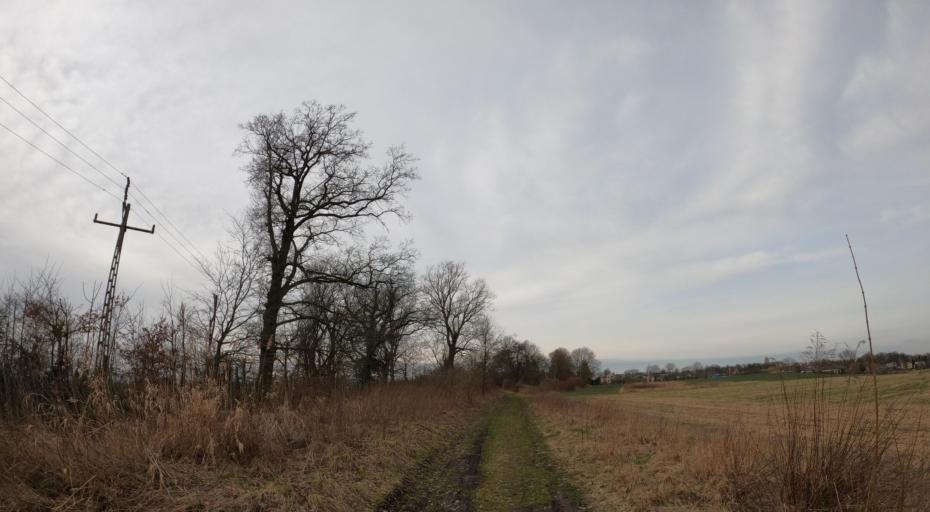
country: PL
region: West Pomeranian Voivodeship
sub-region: Powiat pyrzycki
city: Pyrzyce
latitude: 53.1328
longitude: 14.9029
